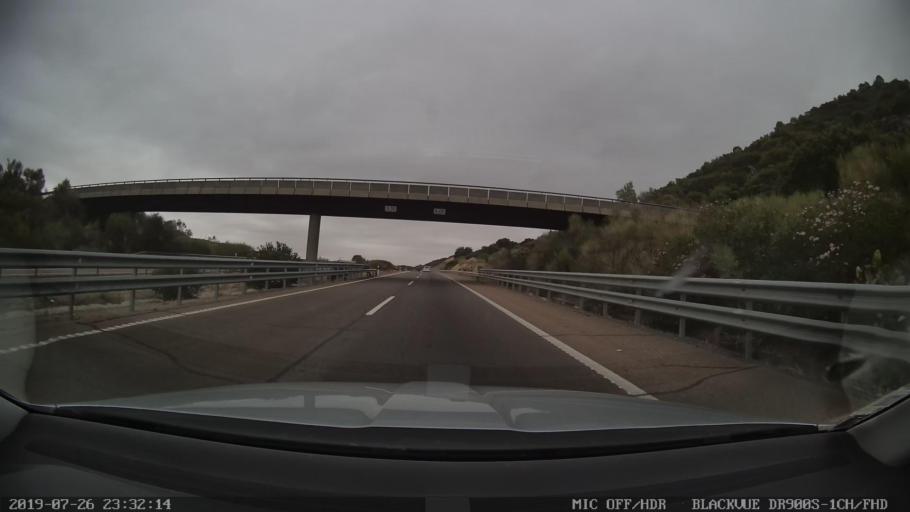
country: ES
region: Extremadura
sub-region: Provincia de Caceres
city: Puerto de Santa Cruz
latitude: 39.3148
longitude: -5.8562
